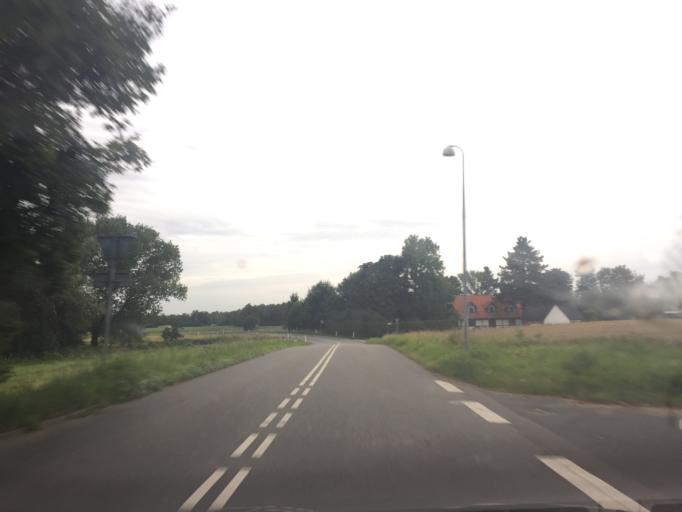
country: DK
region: Capital Region
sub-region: Egedal Kommune
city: Stenlose
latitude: 55.7283
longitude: 12.2043
